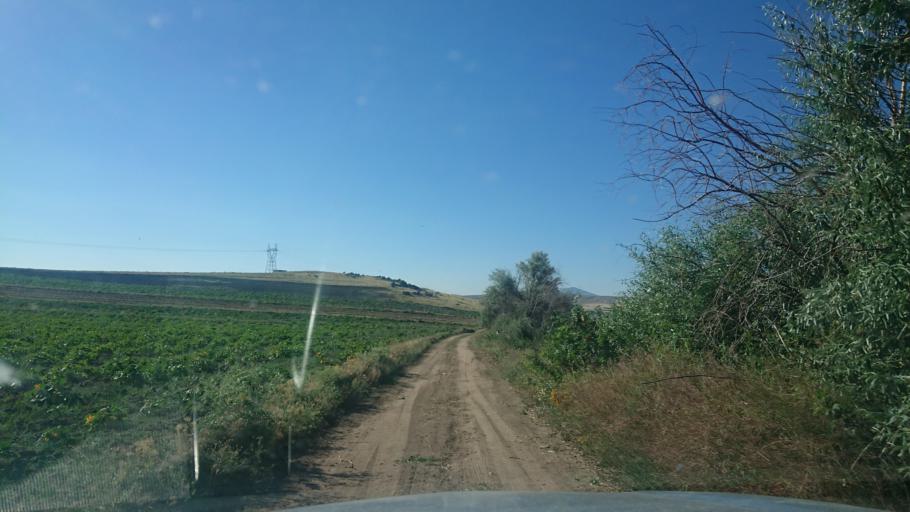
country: TR
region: Aksaray
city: Agacoren
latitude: 38.8331
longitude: 33.9417
